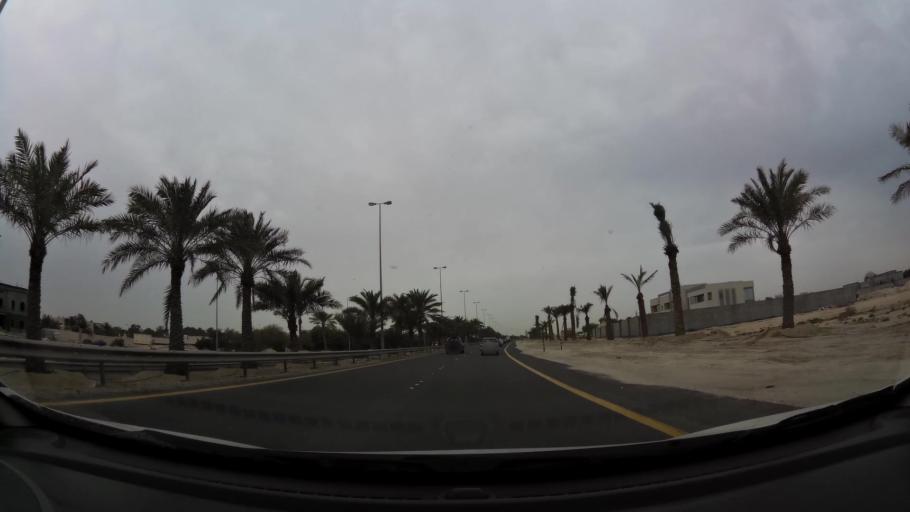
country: BH
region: Northern
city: Ar Rifa'
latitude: 26.1442
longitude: 50.5399
